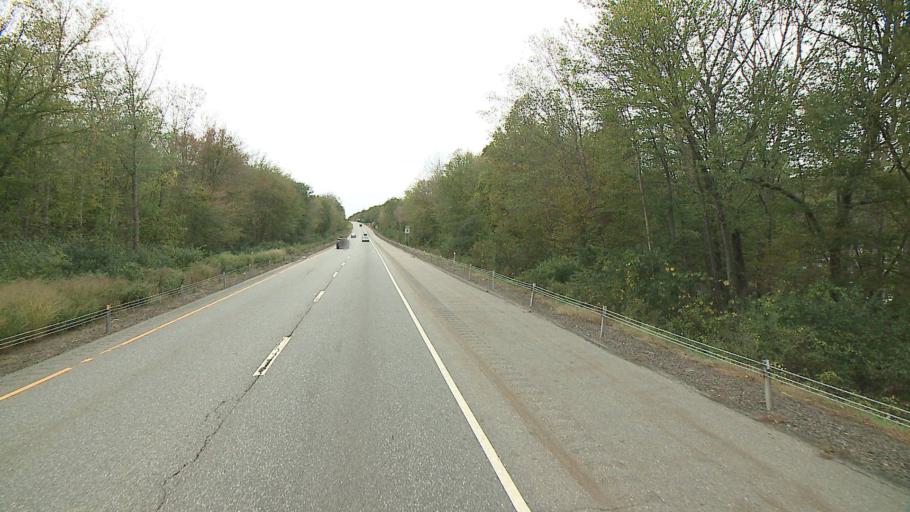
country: US
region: Connecticut
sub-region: Middlesex County
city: Deep River Center
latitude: 41.3851
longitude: -72.4501
